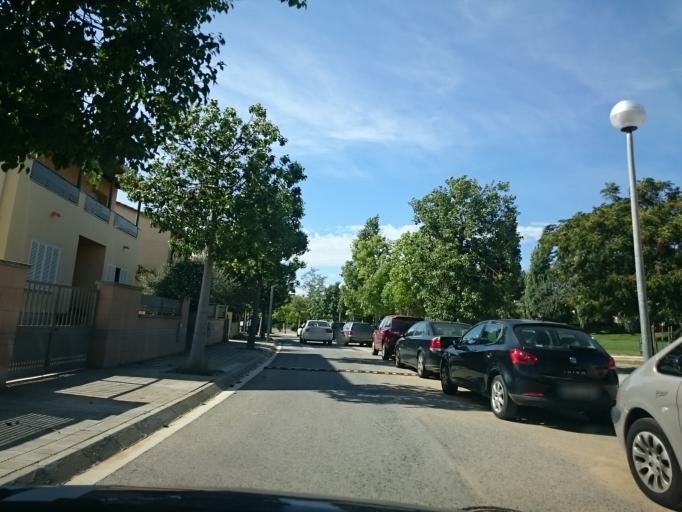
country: ES
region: Catalonia
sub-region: Provincia de Barcelona
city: Castellet
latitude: 41.2661
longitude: 1.6003
